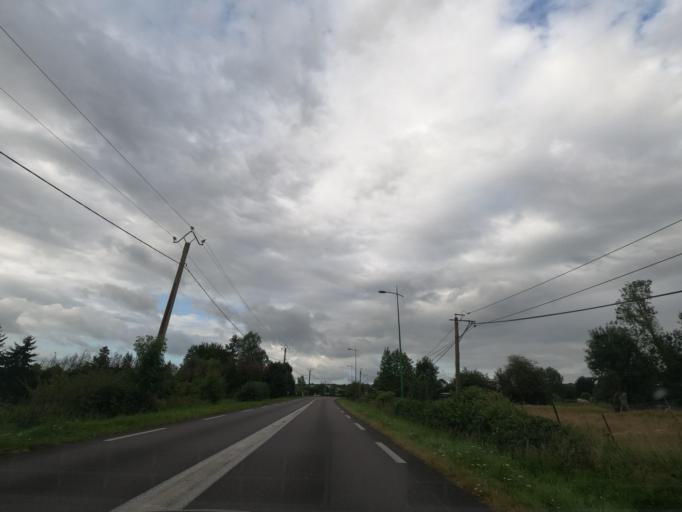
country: FR
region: Haute-Normandie
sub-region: Departement de l'Eure
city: Bourgtheroulde-Infreville
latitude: 49.3078
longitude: 0.8856
